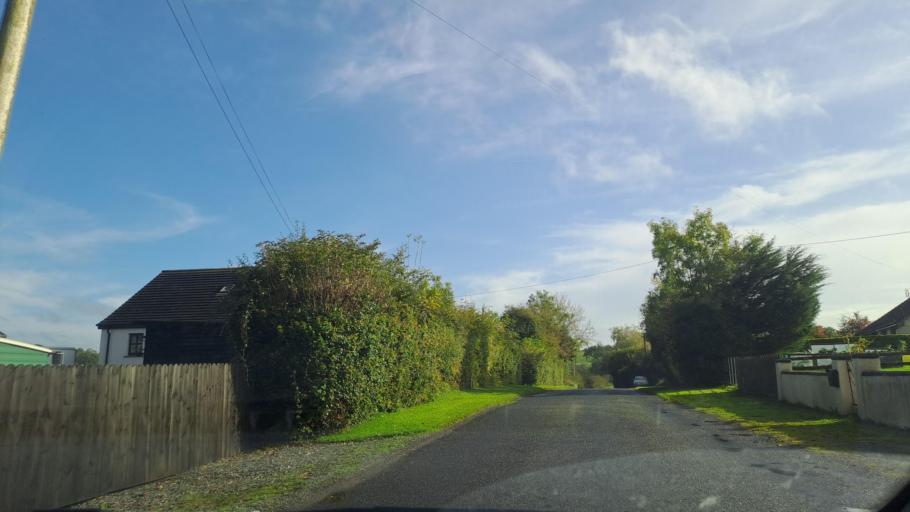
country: IE
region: Ulster
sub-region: County Monaghan
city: Carrickmacross
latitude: 53.8838
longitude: -6.6878
